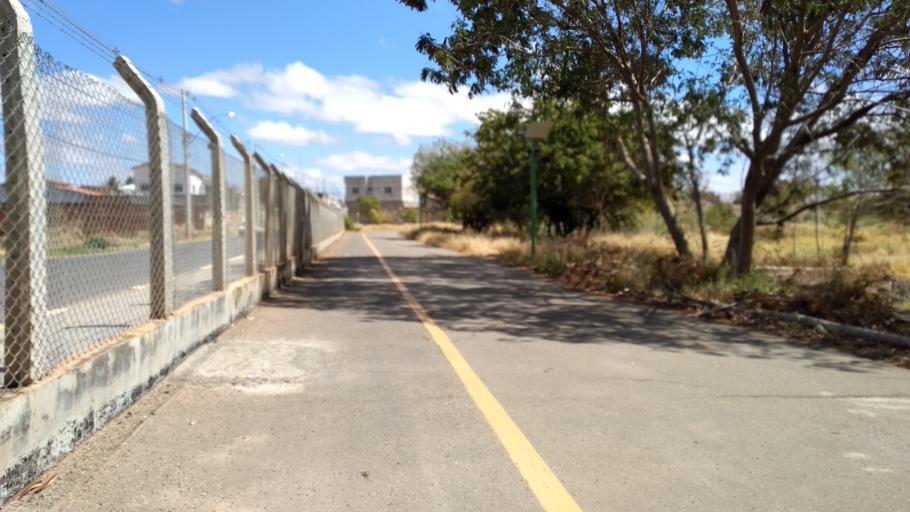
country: BR
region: Bahia
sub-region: Guanambi
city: Guanambi
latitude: -14.2262
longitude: -42.7659
